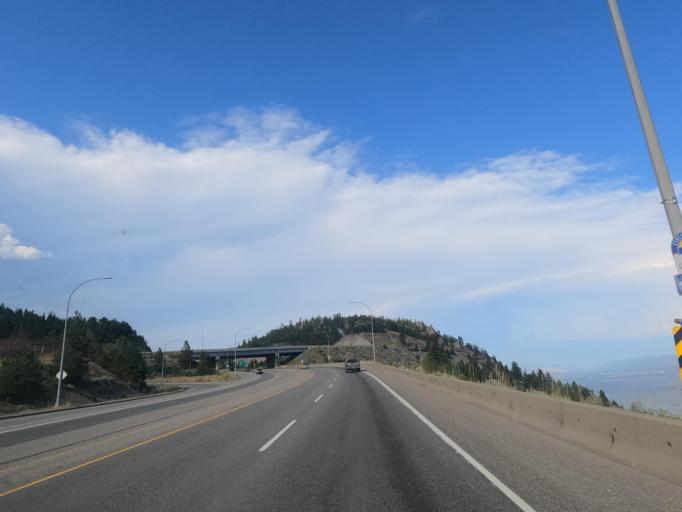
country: CA
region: British Columbia
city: Peachland
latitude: 49.8031
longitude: -119.6669
